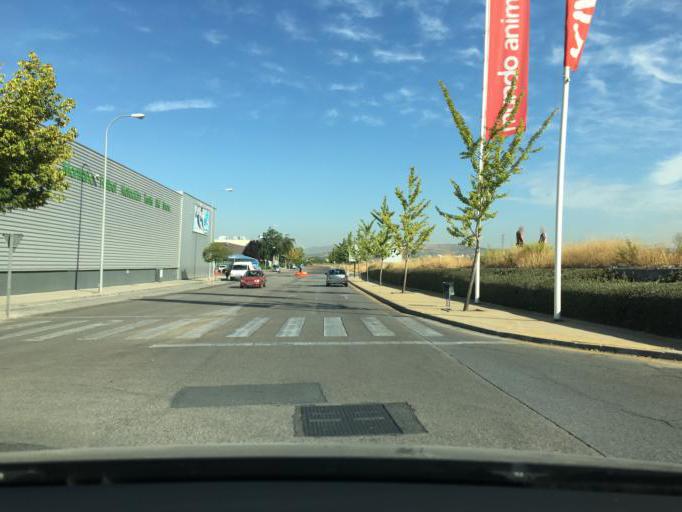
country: ES
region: Andalusia
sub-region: Provincia de Granada
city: Pulianas
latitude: 37.2131
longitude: -3.6149
